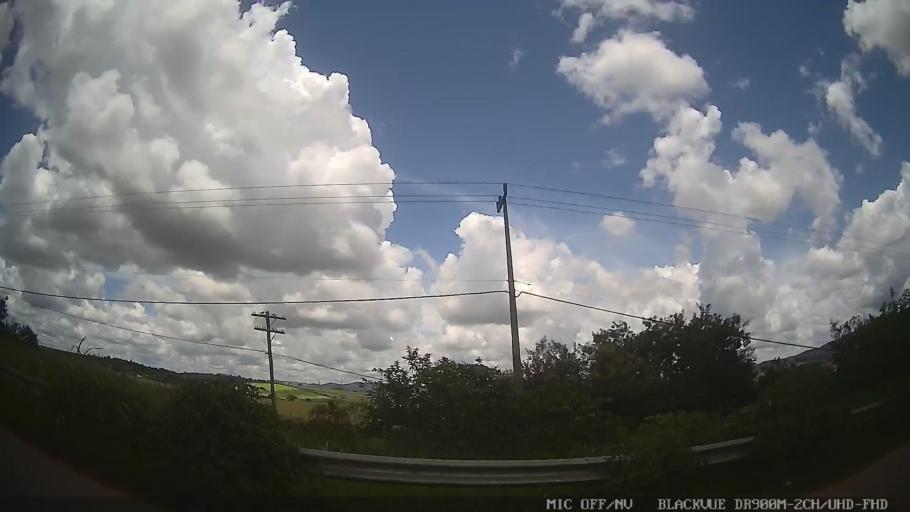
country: BR
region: Sao Paulo
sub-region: Amparo
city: Amparo
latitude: -22.8210
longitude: -46.6844
